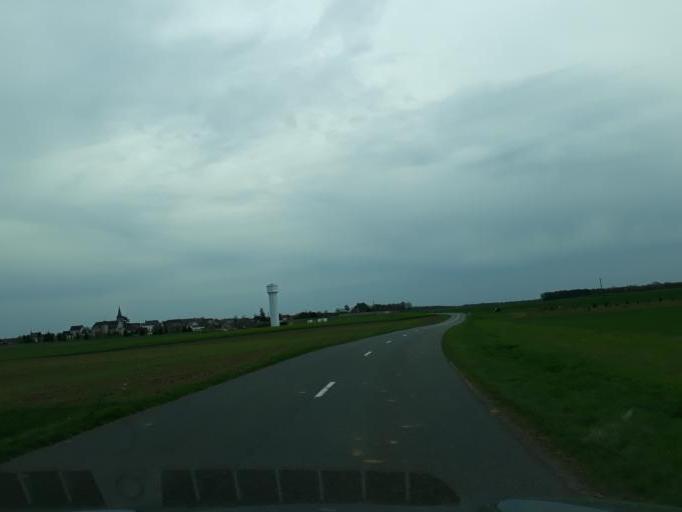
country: FR
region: Centre
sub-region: Departement du Loiret
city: Epieds-en-Beauce
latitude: 47.8968
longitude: 1.6211
